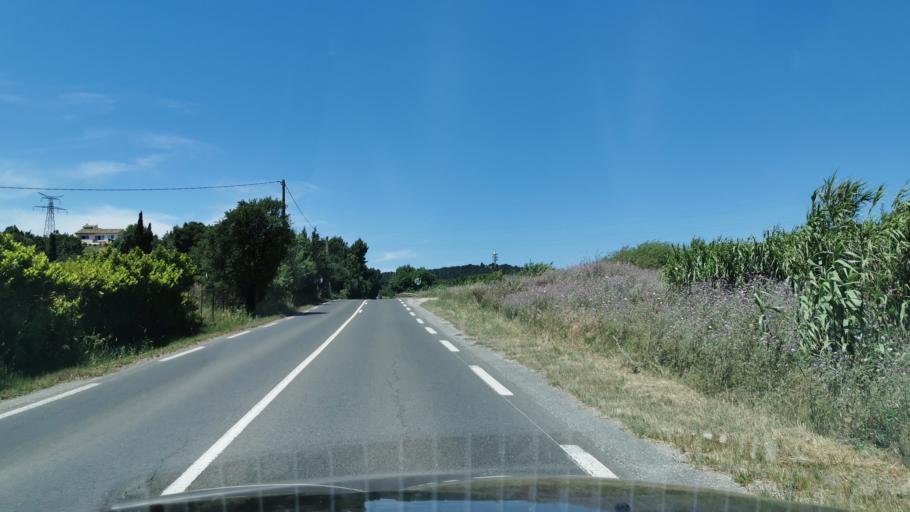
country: FR
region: Languedoc-Roussillon
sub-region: Departement de l'Aude
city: Moussan
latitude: 43.2008
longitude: 2.9686
